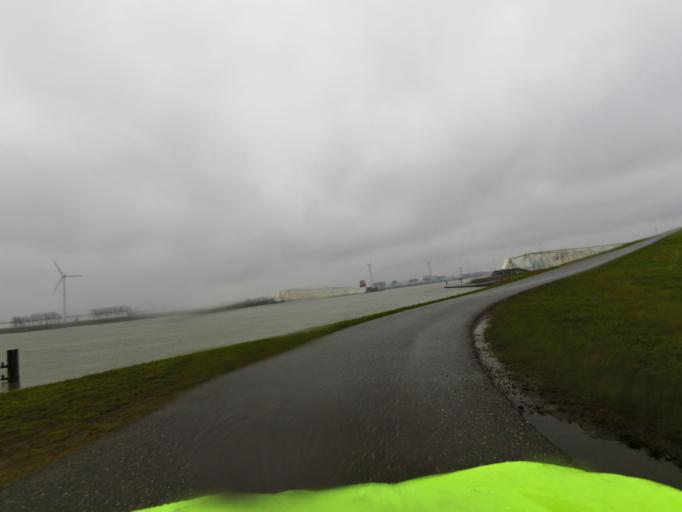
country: NL
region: South Holland
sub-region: Gemeente Westland
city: Maasdijk
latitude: 51.9542
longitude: 4.1716
